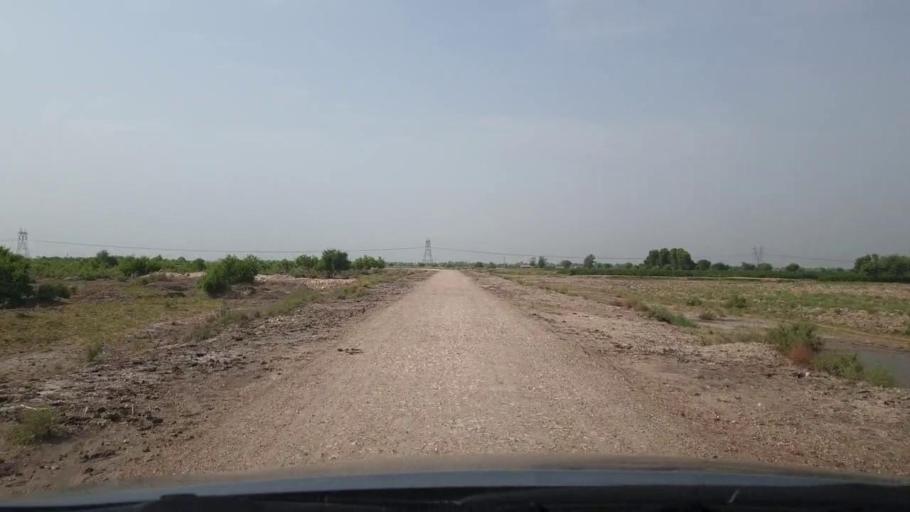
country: PK
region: Sindh
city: Rohri
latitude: 27.6806
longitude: 69.0121
